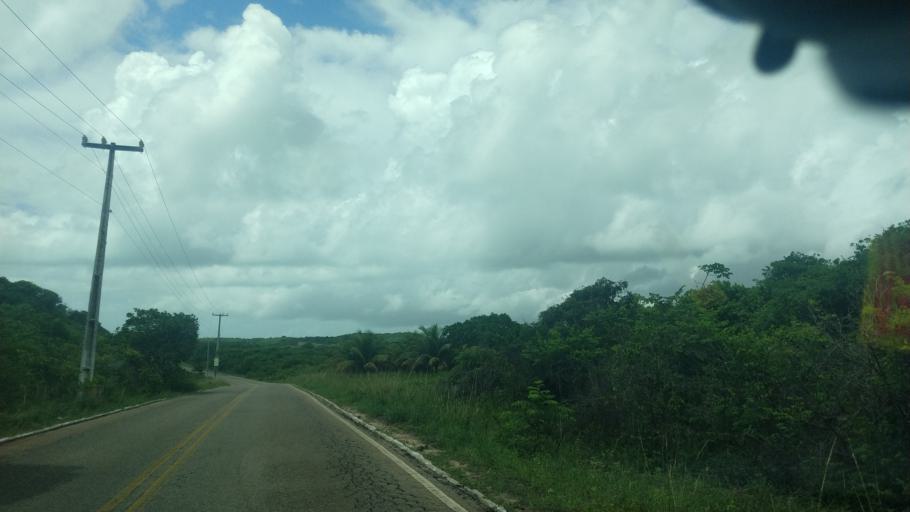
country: BR
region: Rio Grande do Norte
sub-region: Nisia Floresta
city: Nisia Floresta
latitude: -6.0474
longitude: -35.1127
